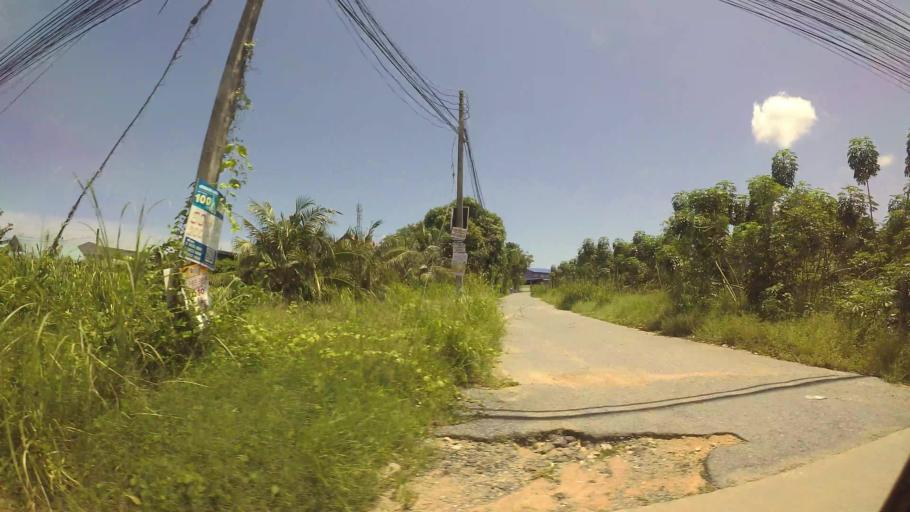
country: TH
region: Chon Buri
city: Si Racha
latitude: 13.1322
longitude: 100.9549
